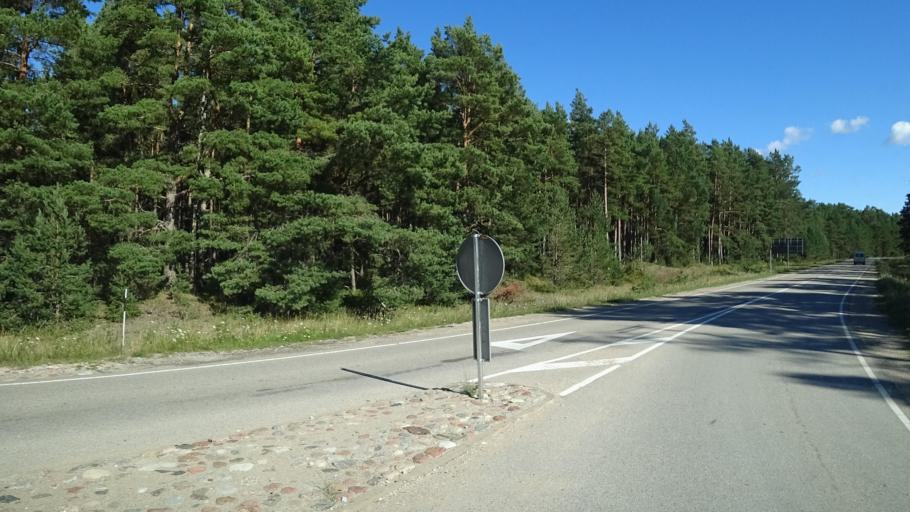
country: LV
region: Rojas
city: Roja
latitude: 57.7549
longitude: 22.5940
